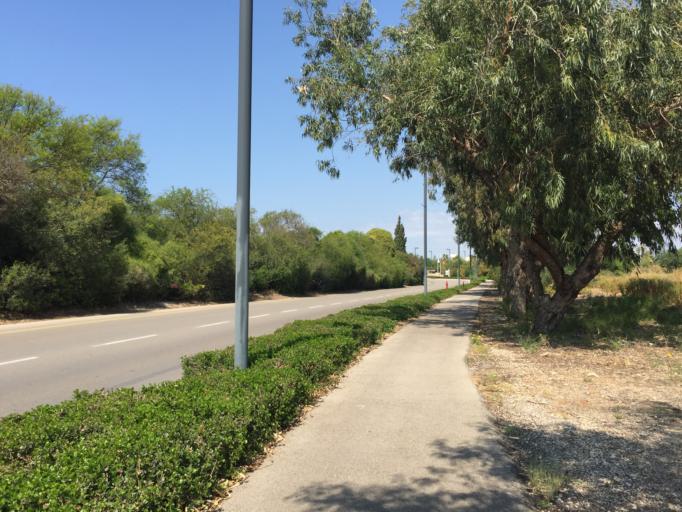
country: IL
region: Haifa
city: Qesarya
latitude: 32.5007
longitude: 34.9042
